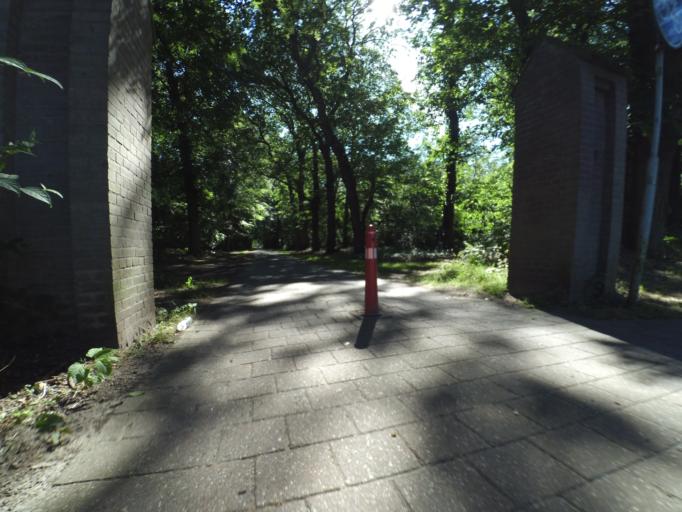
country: NL
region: Utrecht
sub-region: Gemeente Utrechtse Heuvelrug
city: Driebergen-Rijsenburg
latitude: 52.0591
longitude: 5.2891
